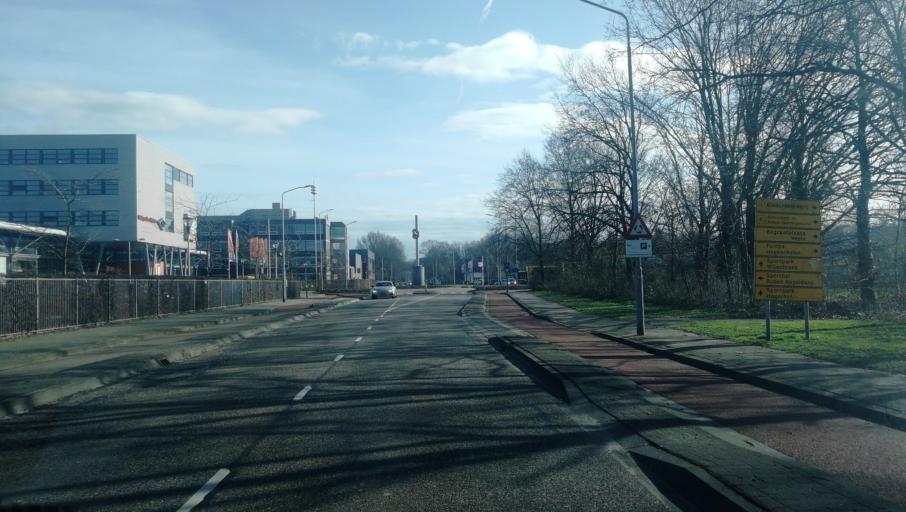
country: NL
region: Limburg
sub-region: Gemeente Venlo
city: Venlo
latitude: 51.3571
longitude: 6.1608
